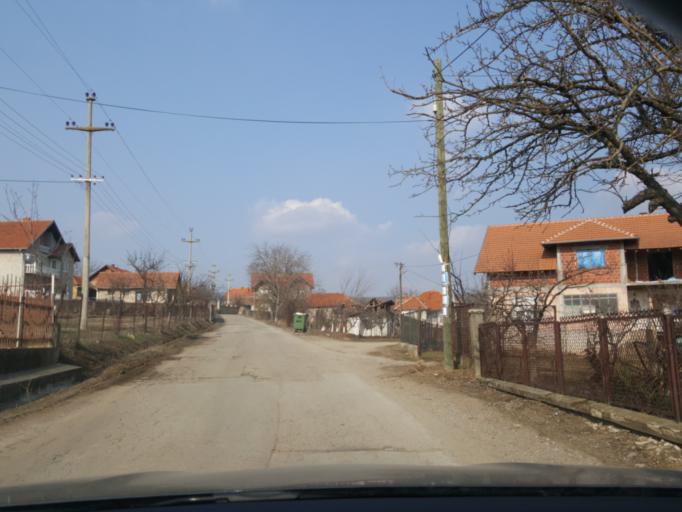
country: RS
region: Central Serbia
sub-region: Nisavski Okrug
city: Aleksinac
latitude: 43.5261
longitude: 21.7353
